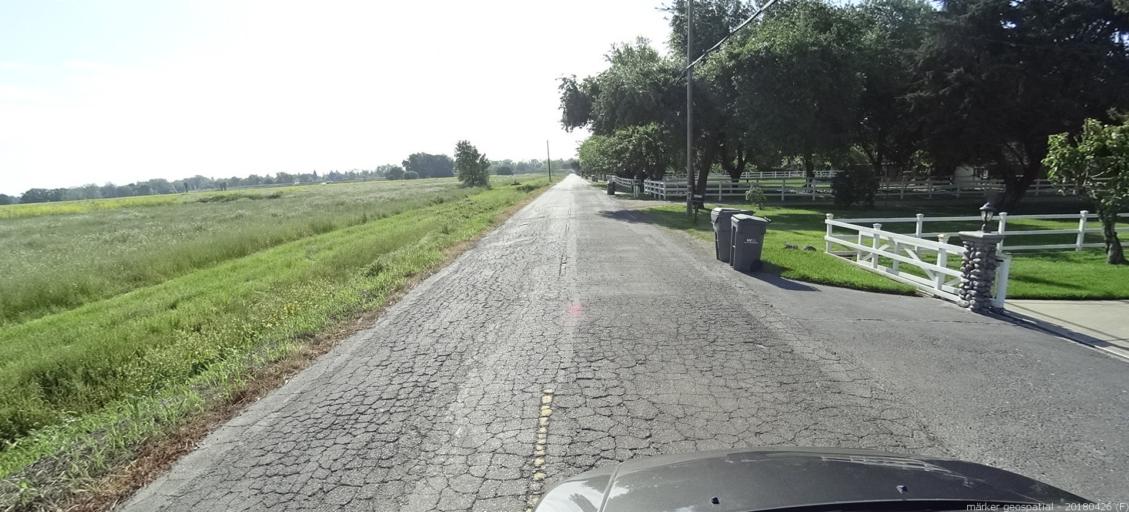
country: US
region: California
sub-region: Yolo County
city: West Sacramento
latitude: 38.5310
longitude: -121.5410
